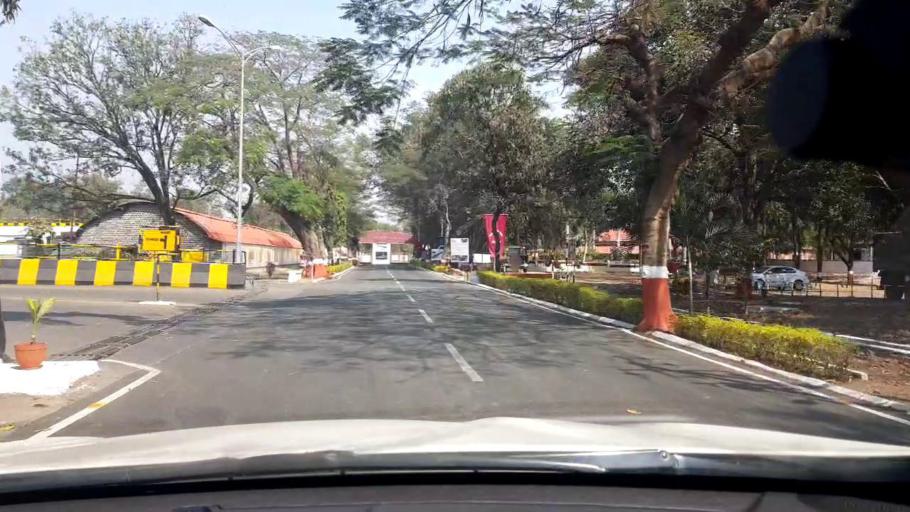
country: IN
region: Maharashtra
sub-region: Pune Division
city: Khadki
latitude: 18.5514
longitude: 73.8638
